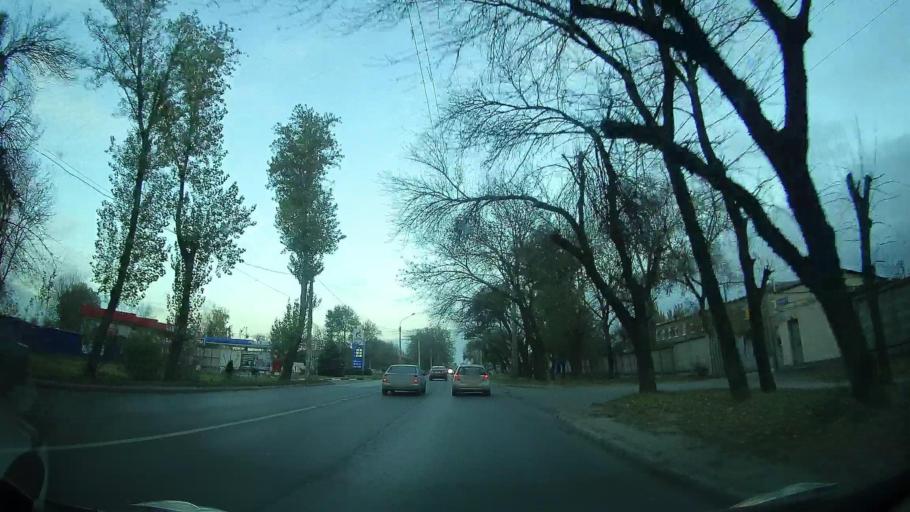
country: RU
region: Rostov
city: Severnyy
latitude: 47.2579
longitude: 39.6350
